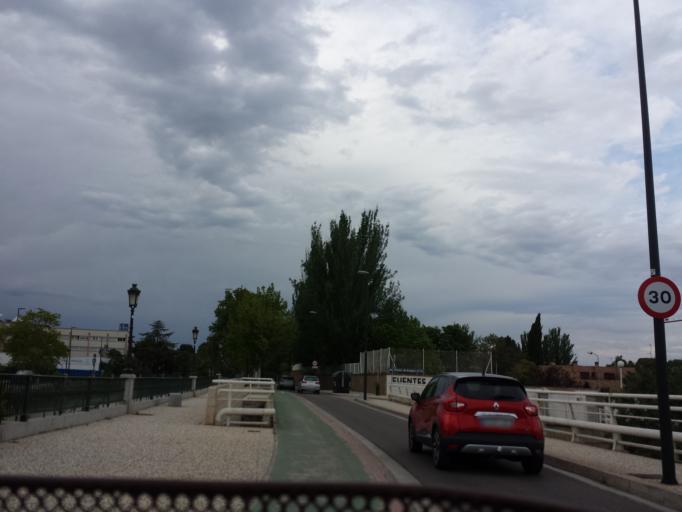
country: ES
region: Aragon
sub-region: Provincia de Zaragoza
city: Delicias
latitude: 41.6223
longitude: -0.9049
